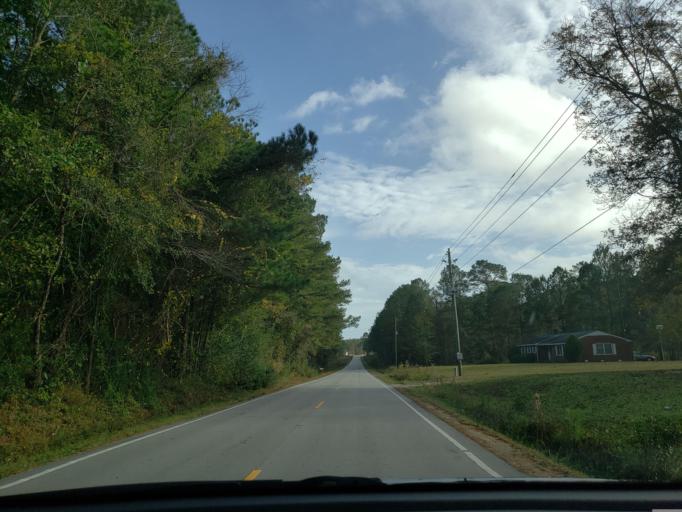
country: US
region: North Carolina
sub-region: Onslow County
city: Jacksonville
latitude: 34.6844
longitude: -77.5078
